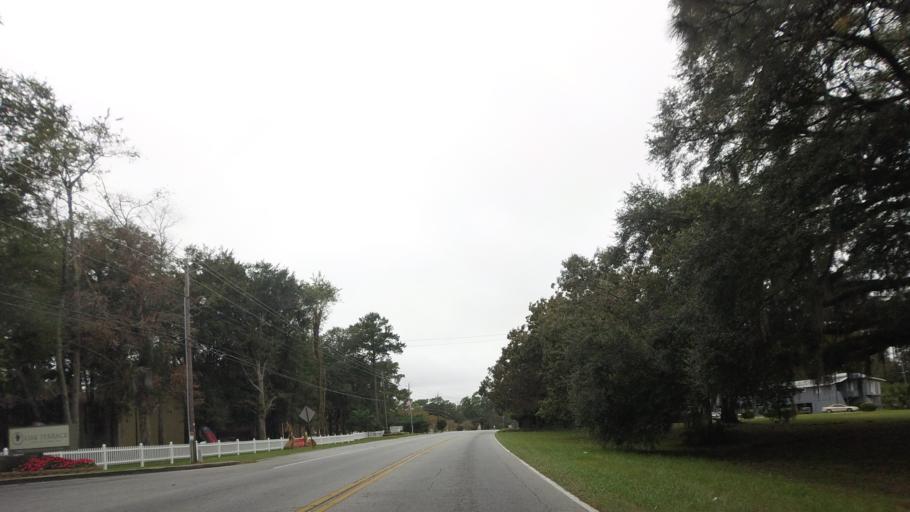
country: US
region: Georgia
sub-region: Lowndes County
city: Valdosta
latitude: 30.8577
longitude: -83.2619
